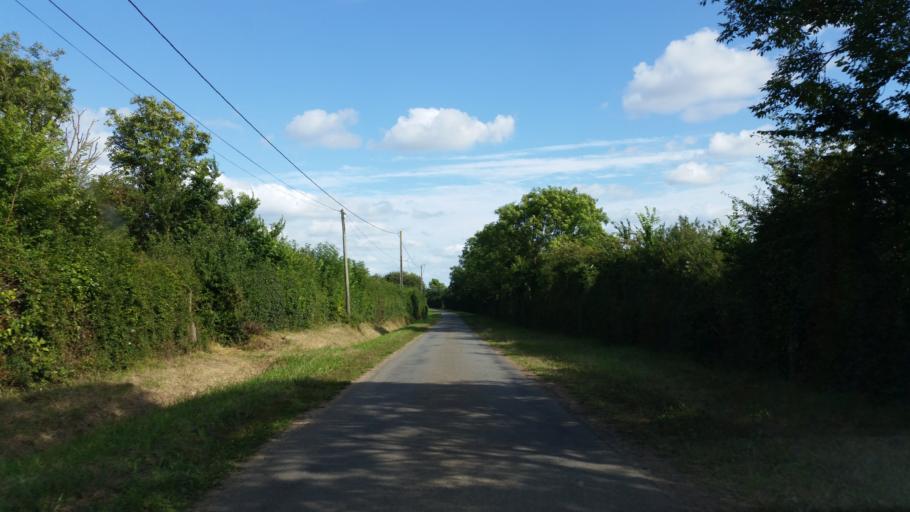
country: FR
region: Lower Normandy
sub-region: Departement de la Manche
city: Sainte-Mere-Eglise
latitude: 49.4601
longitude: -1.2994
